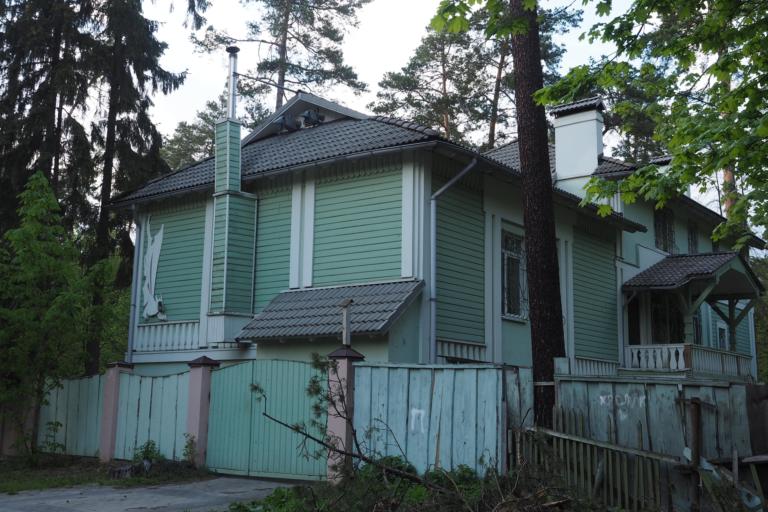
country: RU
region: Moskovskaya
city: Kratovo
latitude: 55.5976
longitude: 38.1587
